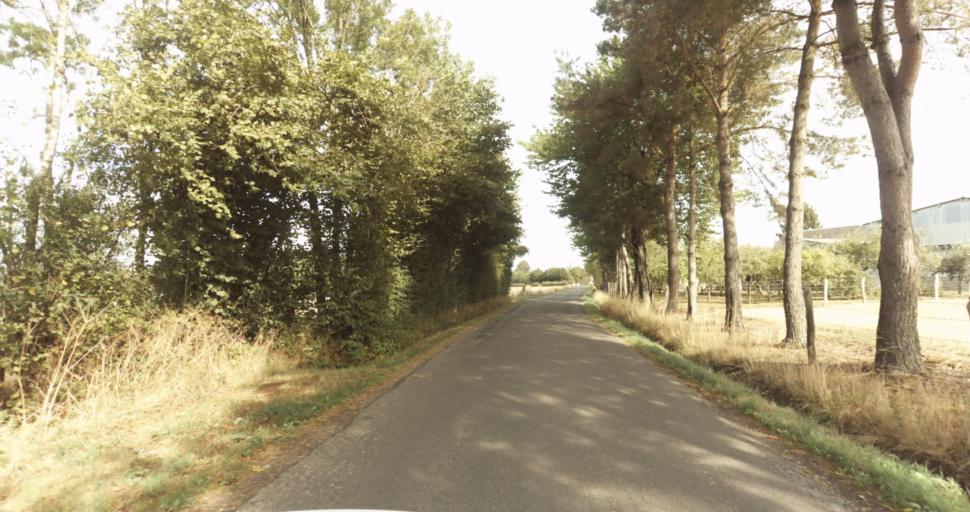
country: FR
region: Lower Normandy
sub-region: Departement de l'Orne
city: Gace
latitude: 48.8251
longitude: 0.3830
